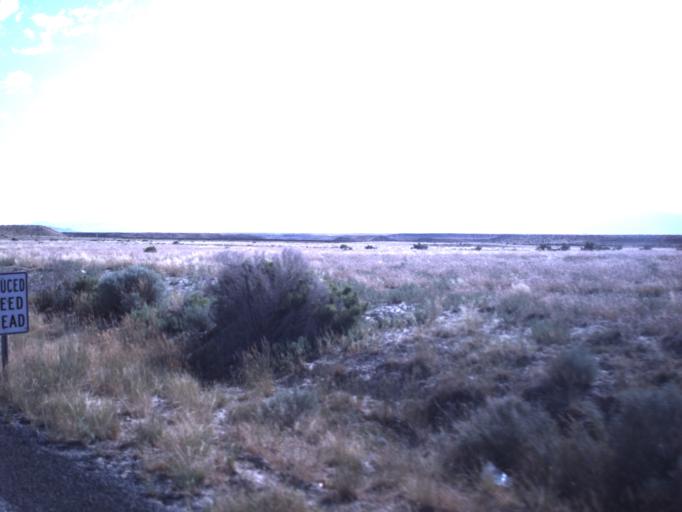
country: US
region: Utah
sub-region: Millard County
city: Fillmore
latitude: 38.8975
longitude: -112.8237
